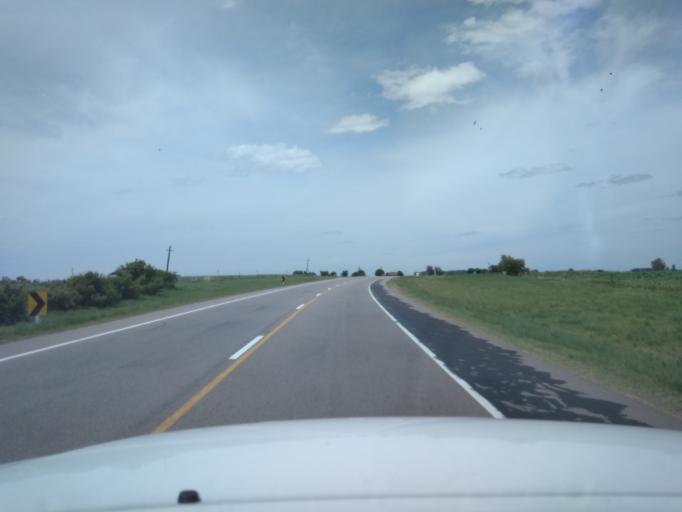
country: UY
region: Florida
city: Cardal
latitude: -34.3177
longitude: -56.2422
